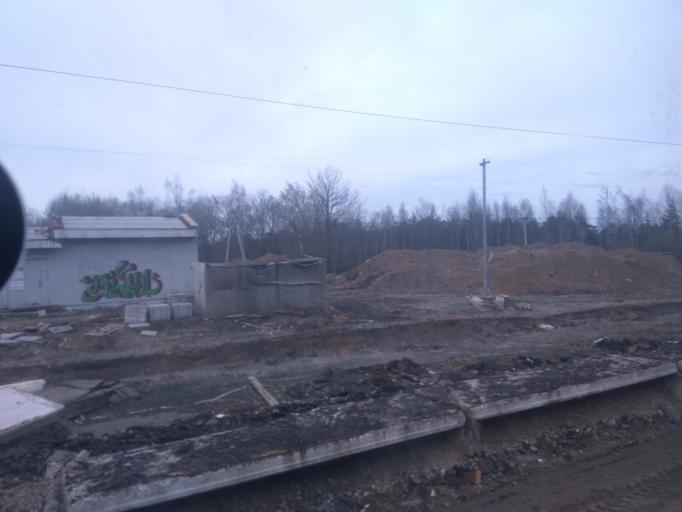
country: RU
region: Moskovskaya
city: Semkhoz
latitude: 56.3435
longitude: 38.0712
